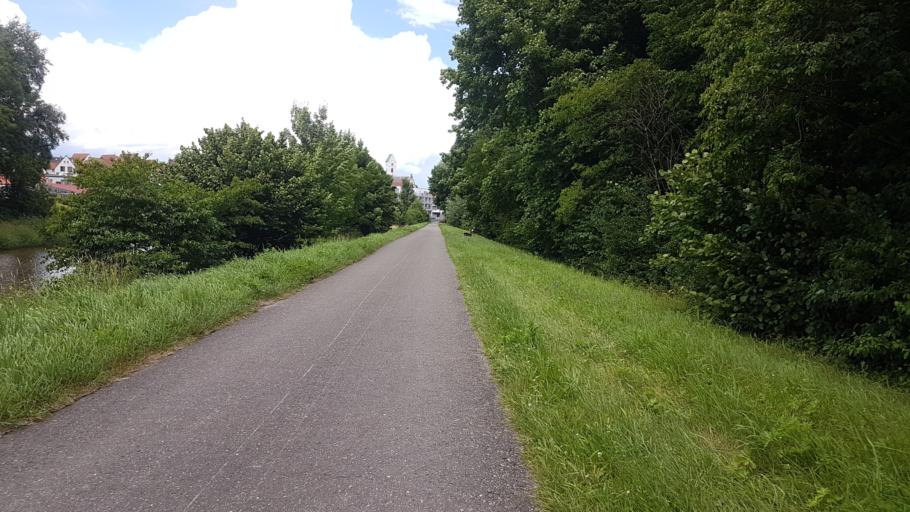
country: DE
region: Baden-Wuerttemberg
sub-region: Tuebingen Region
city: Riedlingen
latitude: 48.1490
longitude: 9.4765
